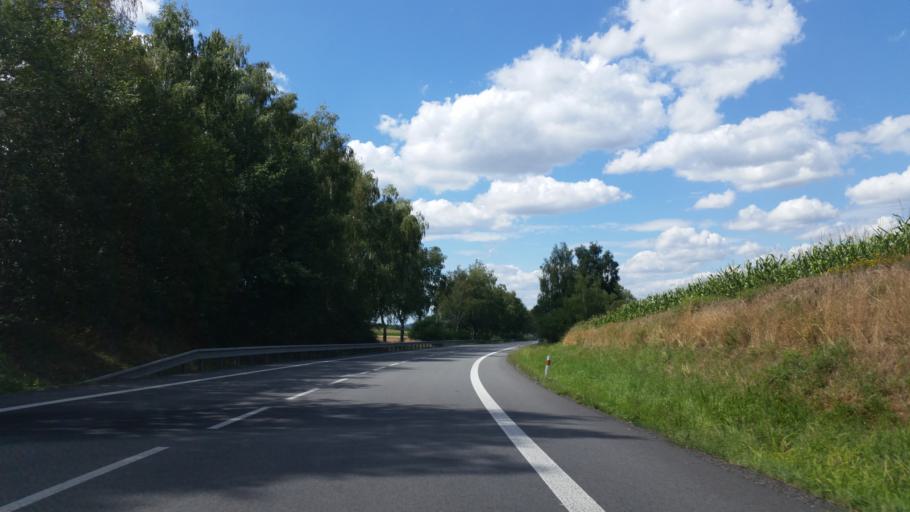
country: CZ
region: Vysocina
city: Nova Cerekev
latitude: 49.4212
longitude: 15.0536
